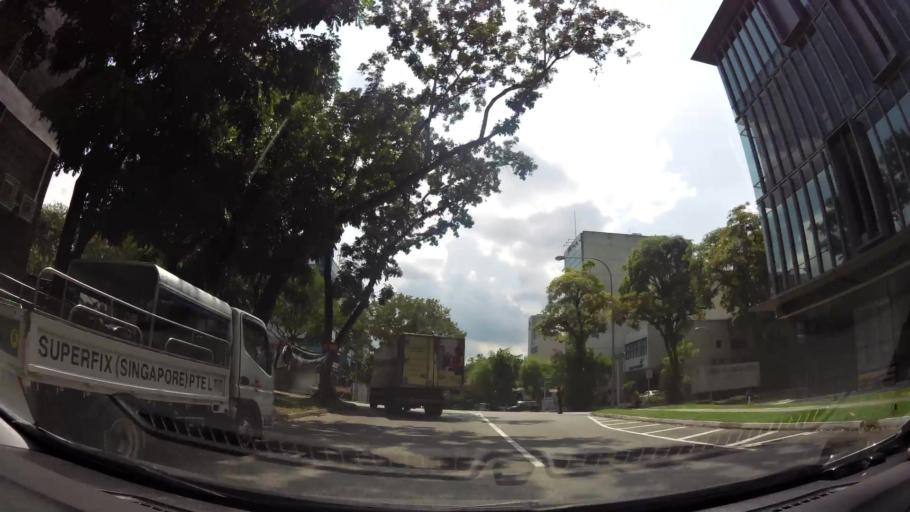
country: SG
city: Singapore
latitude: 1.3843
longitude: 103.8276
